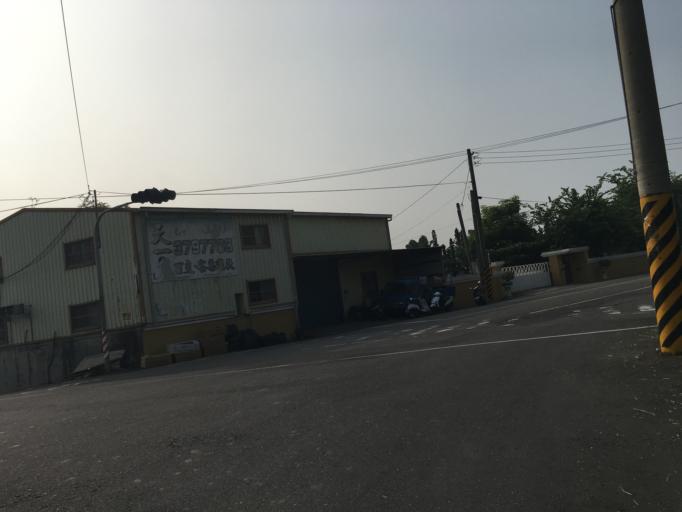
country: TW
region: Taiwan
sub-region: Chiayi
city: Taibao
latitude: 23.4057
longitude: 120.3328
